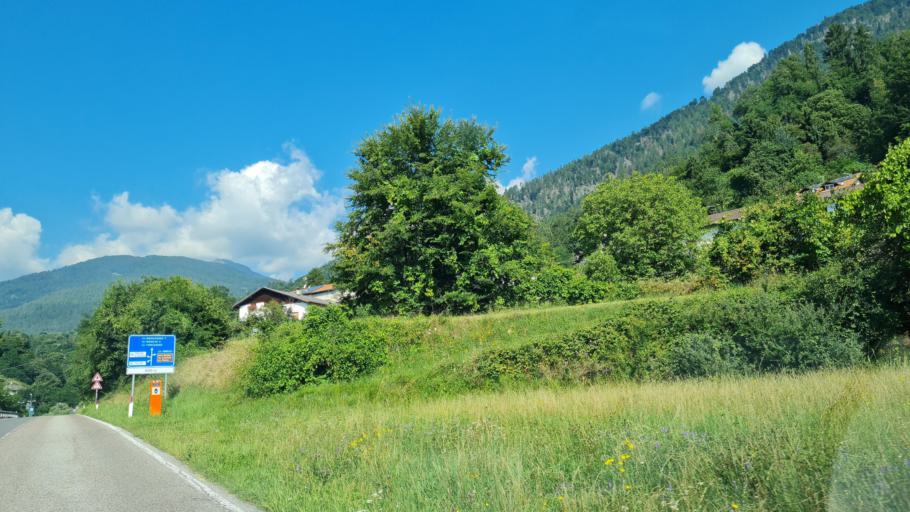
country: IT
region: Trentino-Alto Adige
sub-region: Provincia di Trento
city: Telve
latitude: 46.0749
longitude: 11.4771
